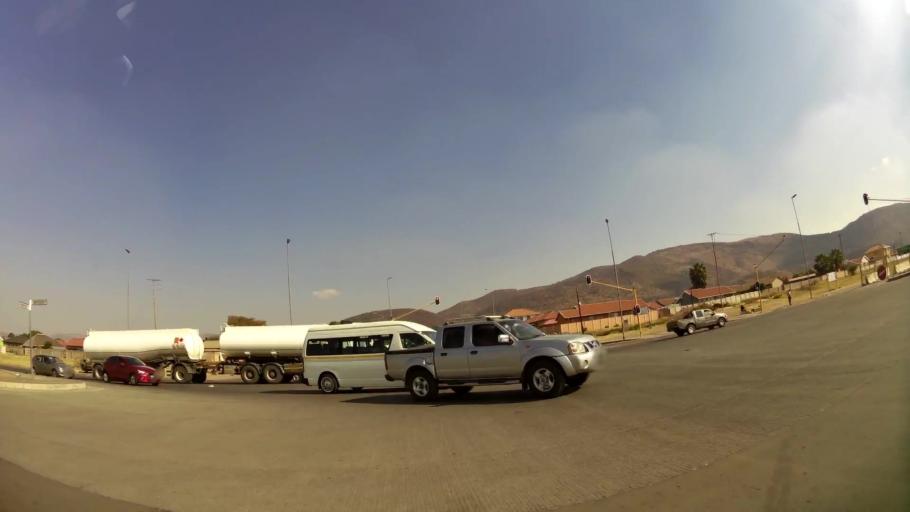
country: ZA
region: North-West
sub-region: Bojanala Platinum District Municipality
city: Rustenburg
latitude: -25.6456
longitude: 27.2097
